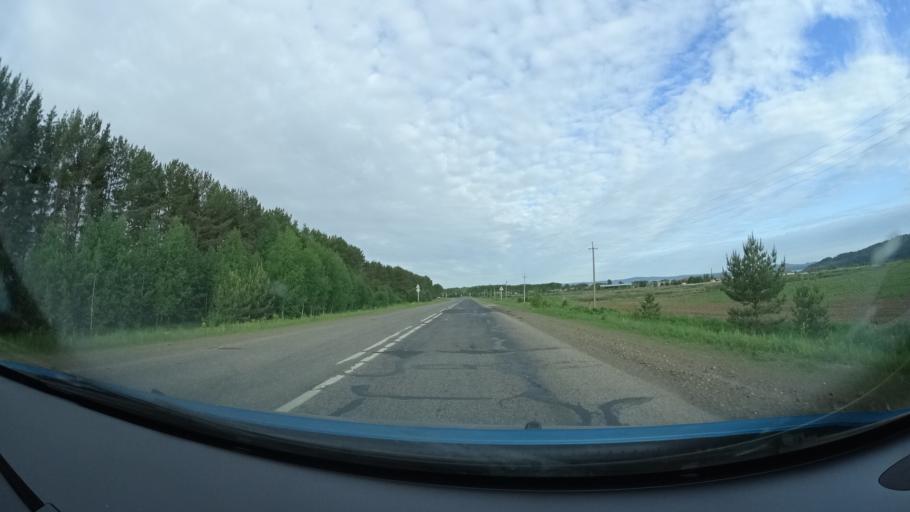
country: RU
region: Perm
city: Osa
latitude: 57.2900
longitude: 55.5888
